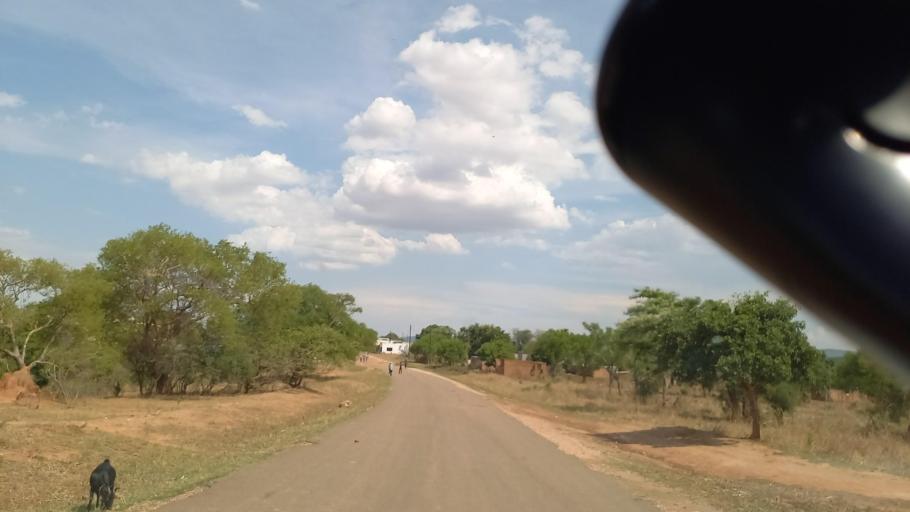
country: ZM
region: Lusaka
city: Kafue
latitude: -16.1893
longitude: 28.0888
